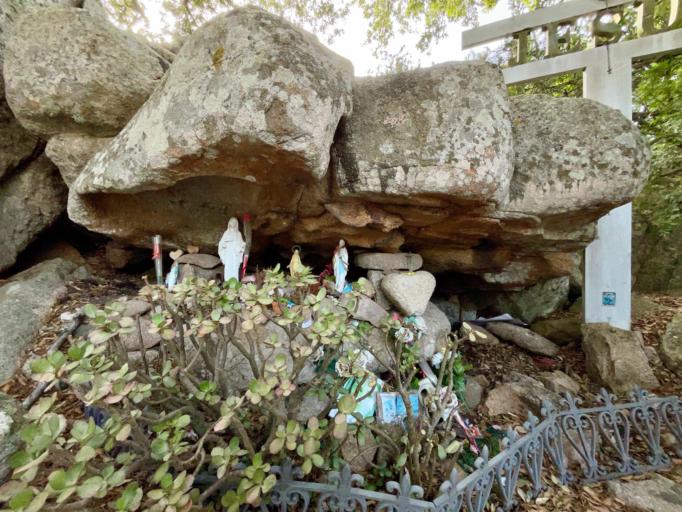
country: IT
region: Sardinia
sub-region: Provincia di Olbia-Tempio
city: La Maddalena
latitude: 41.2080
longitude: 9.4704
